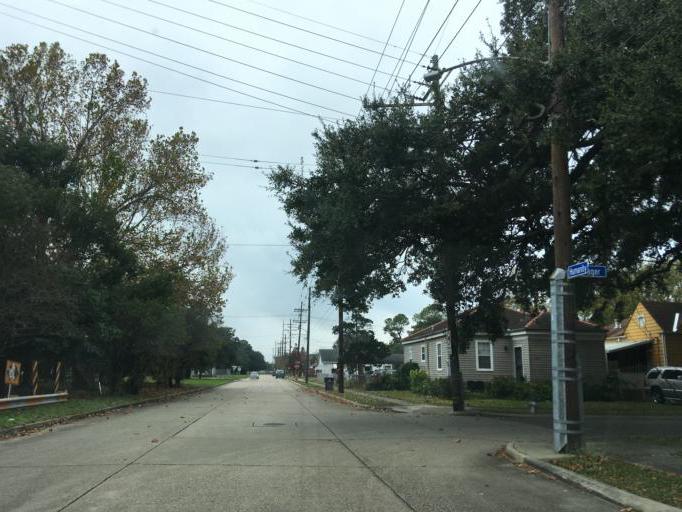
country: US
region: Louisiana
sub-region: Orleans Parish
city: New Orleans
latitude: 29.9917
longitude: -90.0621
